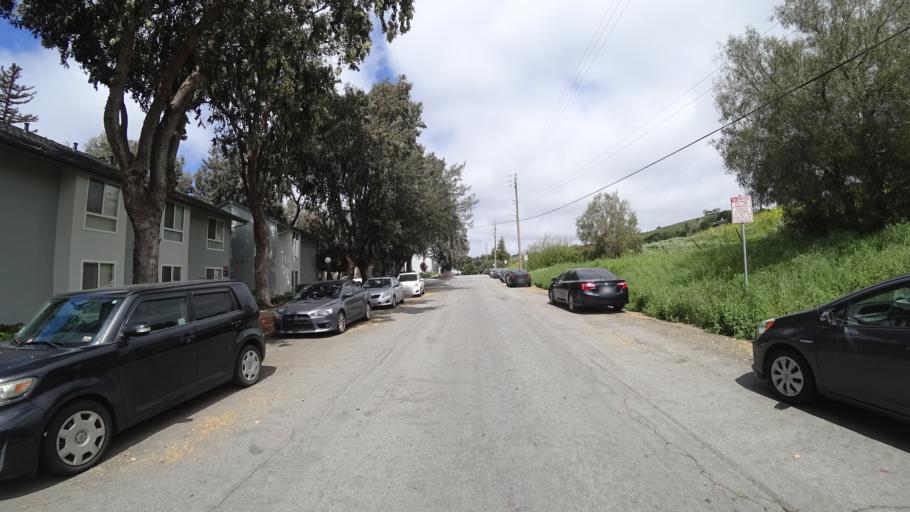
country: US
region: California
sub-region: Alameda County
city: Hayward
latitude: 37.6396
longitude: -122.0541
